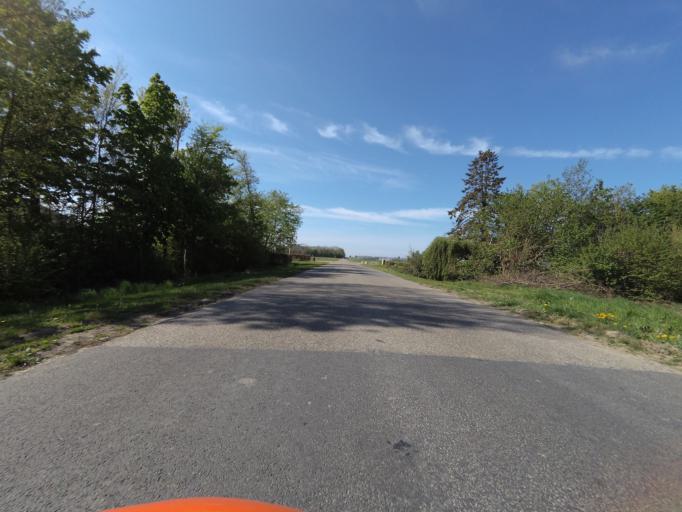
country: NL
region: Flevoland
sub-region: Gemeente Dronten
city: Dronten
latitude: 52.5593
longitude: 5.6821
